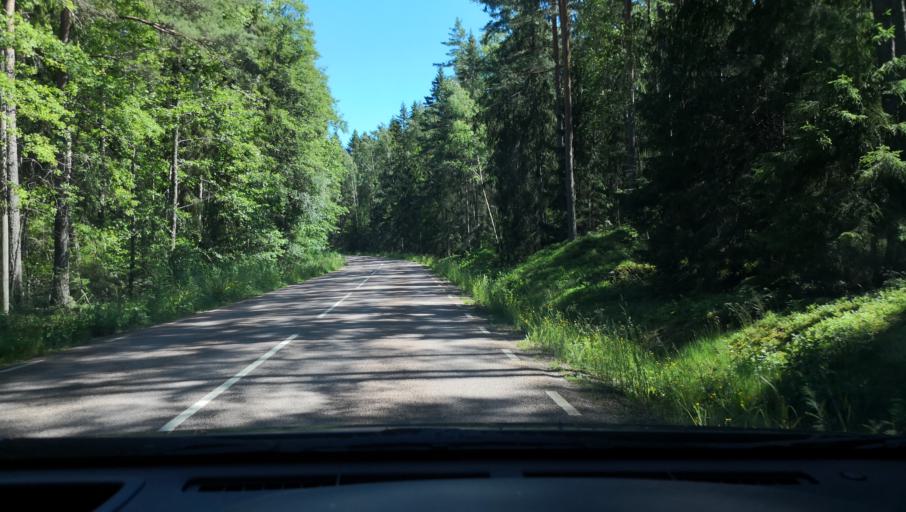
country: SE
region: Vaestmanland
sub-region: Arboga Kommun
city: Tyringe
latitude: 59.2964
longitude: 16.0325
